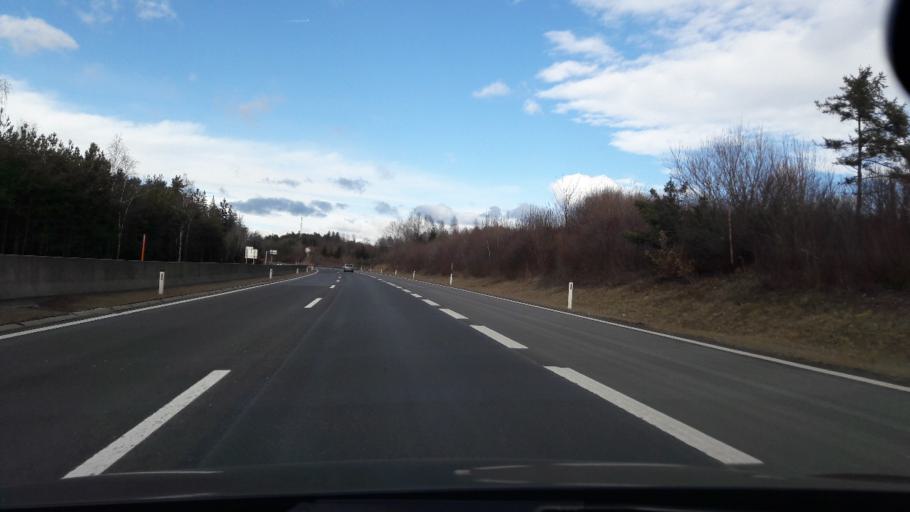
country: AT
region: Burgenland
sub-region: Politischer Bezirk Oberwart
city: Grafenschachen
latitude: 47.3751
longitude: 16.0903
